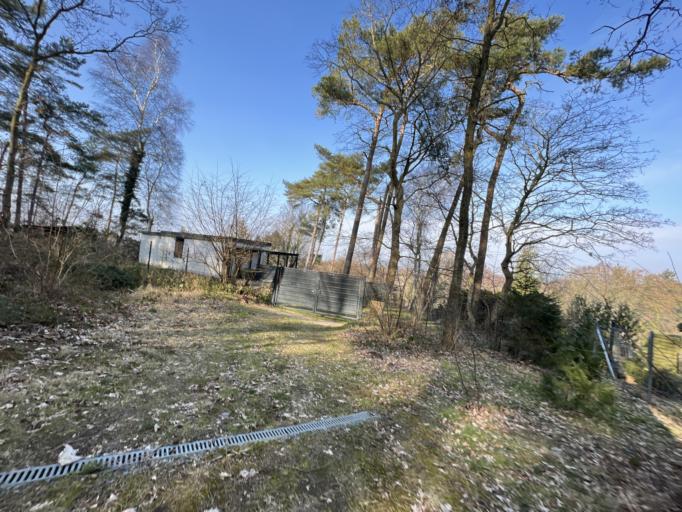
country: DE
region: Mecklenburg-Vorpommern
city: Sagard
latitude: 54.4819
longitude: 13.5602
